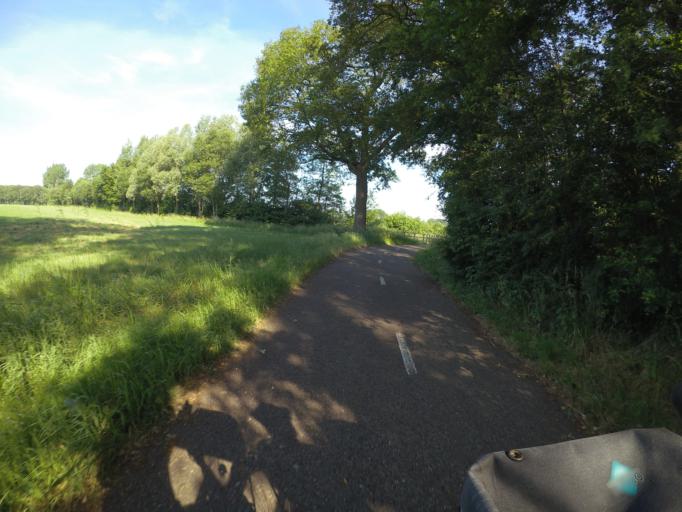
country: NL
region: Gelderland
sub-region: Gemeente Winterswijk
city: Winterswijk
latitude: 52.0010
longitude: 6.7177
